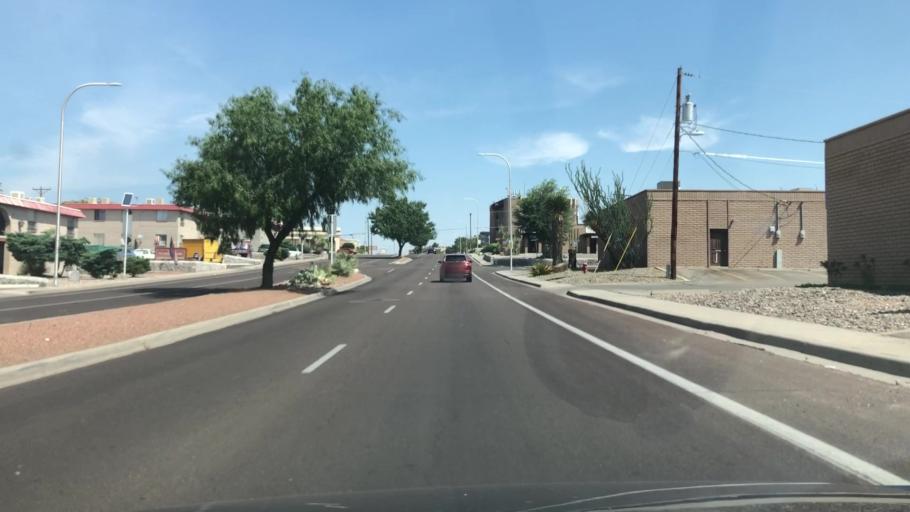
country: US
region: New Mexico
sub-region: Dona Ana County
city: University Park
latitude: 32.3035
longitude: -106.7377
